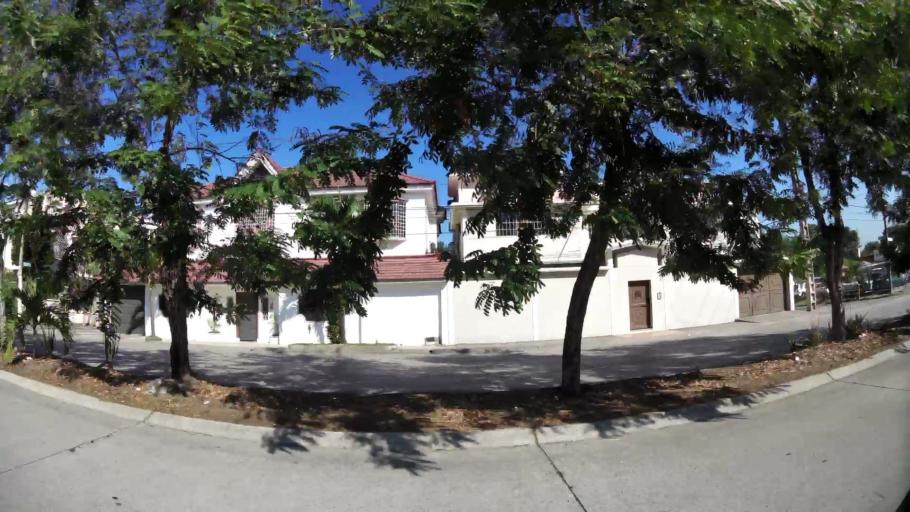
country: EC
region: Guayas
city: Eloy Alfaro
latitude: -2.1547
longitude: -79.9021
